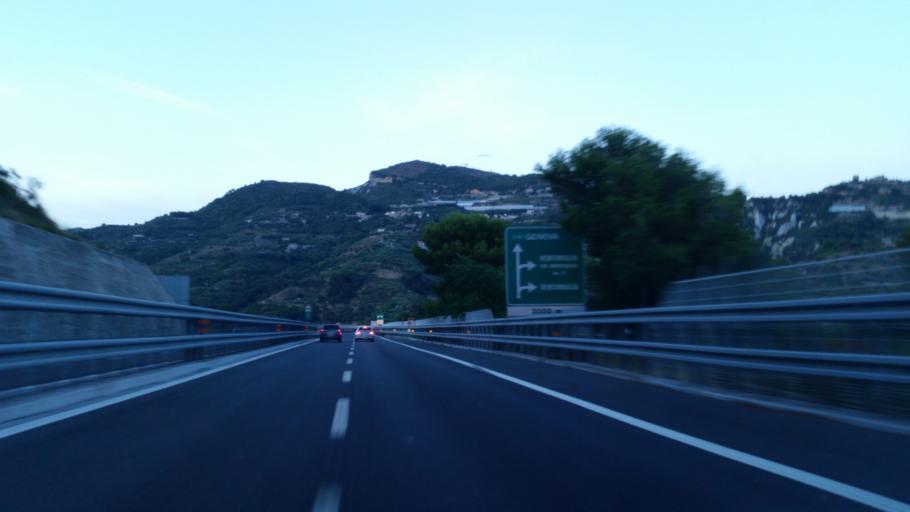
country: IT
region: Liguria
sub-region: Provincia di Imperia
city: Ventimiglia
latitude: 43.7950
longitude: 7.5587
